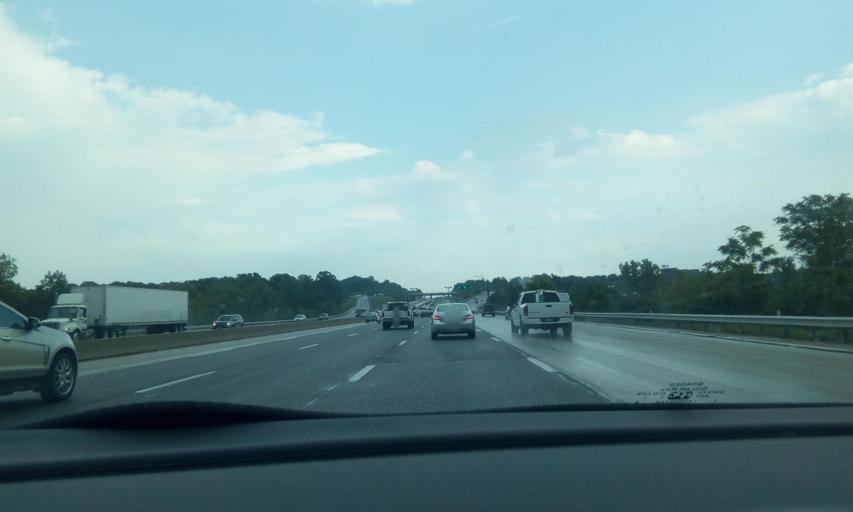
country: US
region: Missouri
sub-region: Saint Louis County
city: Sunset Hills
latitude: 38.5303
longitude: -90.4055
